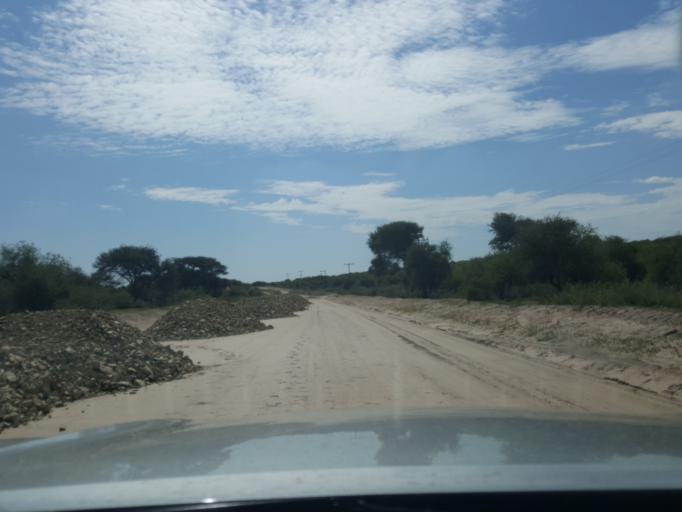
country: BW
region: Kweneng
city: Letlhakeng
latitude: -24.0459
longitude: 25.0175
